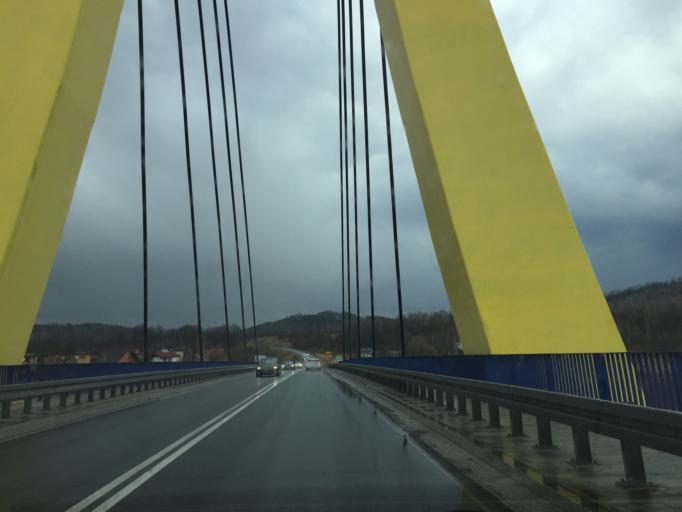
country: PL
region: Lesser Poland Voivodeship
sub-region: Powiat suski
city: Zembrzyce
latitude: 49.7675
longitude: 19.5980
